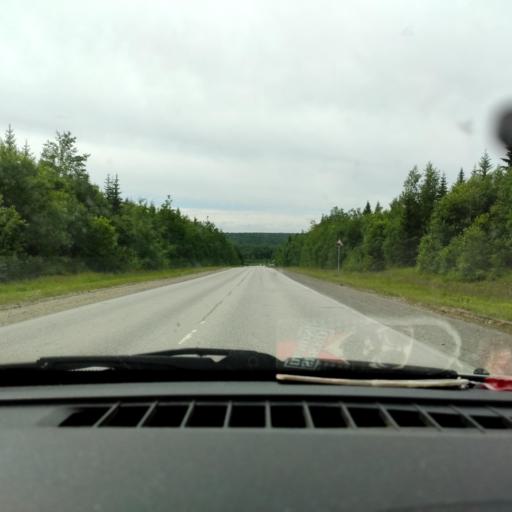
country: RU
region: Perm
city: Chusovoy
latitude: 58.3748
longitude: 57.9587
